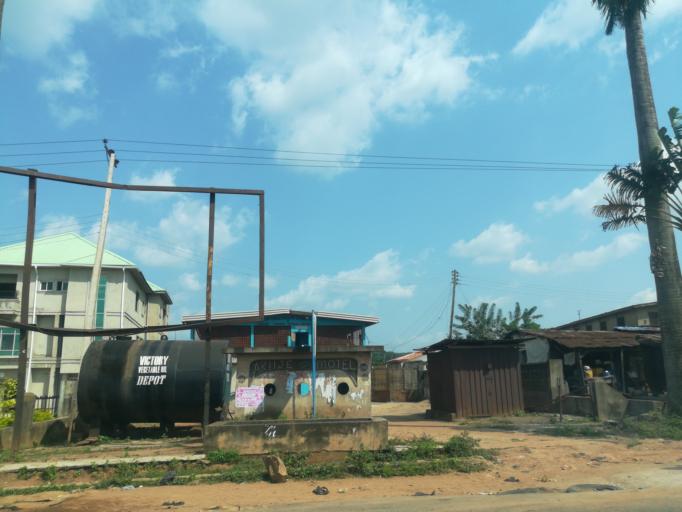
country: NG
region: Oyo
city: Moniya
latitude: 7.5330
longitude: 3.9116
